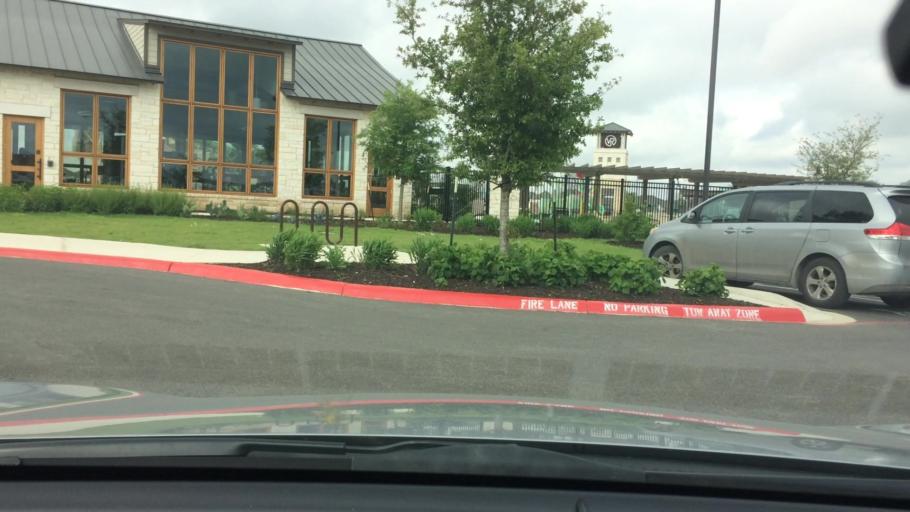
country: US
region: Texas
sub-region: Bexar County
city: Helotes
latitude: 29.5191
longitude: -98.7653
